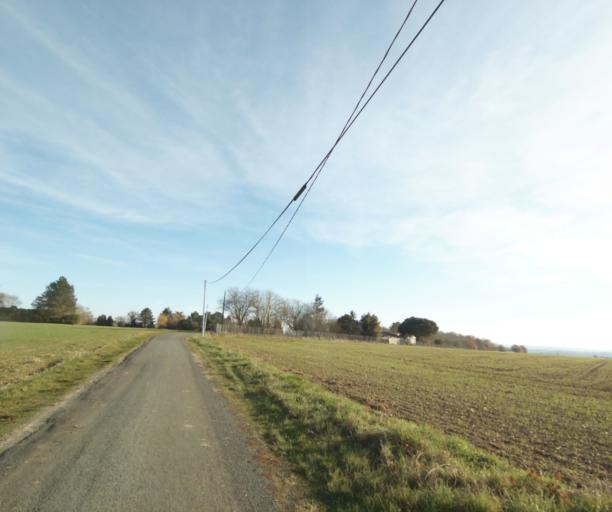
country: FR
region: Poitou-Charentes
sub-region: Departement de la Charente-Maritime
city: Chaniers
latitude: 45.7299
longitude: -0.5456
